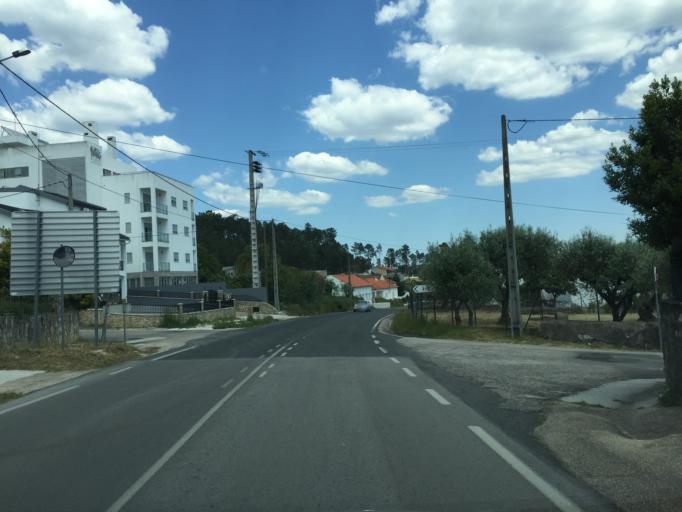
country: PT
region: Santarem
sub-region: Ourem
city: Ourem
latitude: 39.6538
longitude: -8.6058
